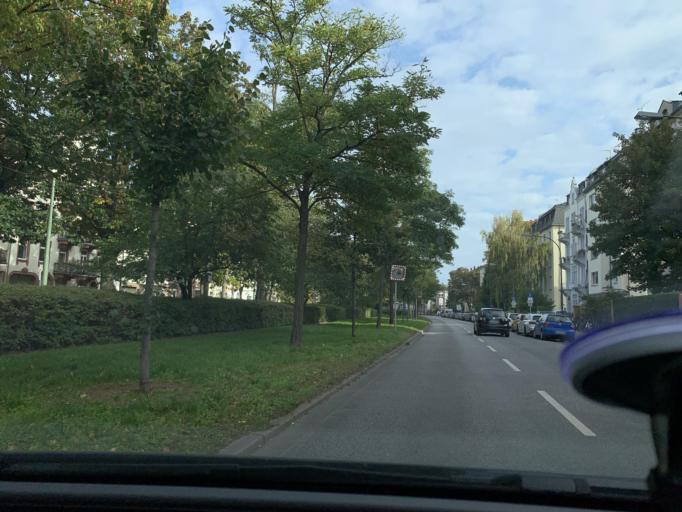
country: DE
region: Hesse
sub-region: Regierungsbezirk Darmstadt
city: Frankfurt am Main
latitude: 50.1212
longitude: 8.7085
